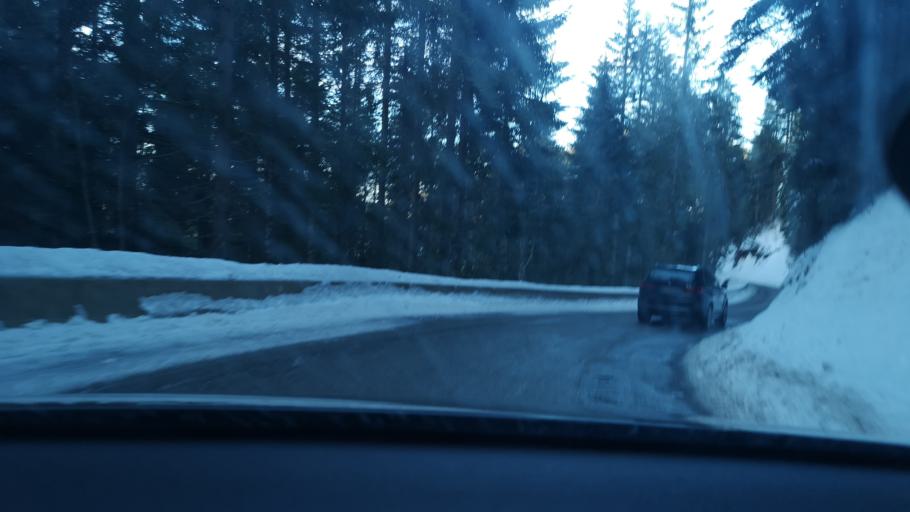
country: FR
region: Franche-Comte
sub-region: Departement du Doubs
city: Montlebon
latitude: 46.9798
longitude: 6.5609
